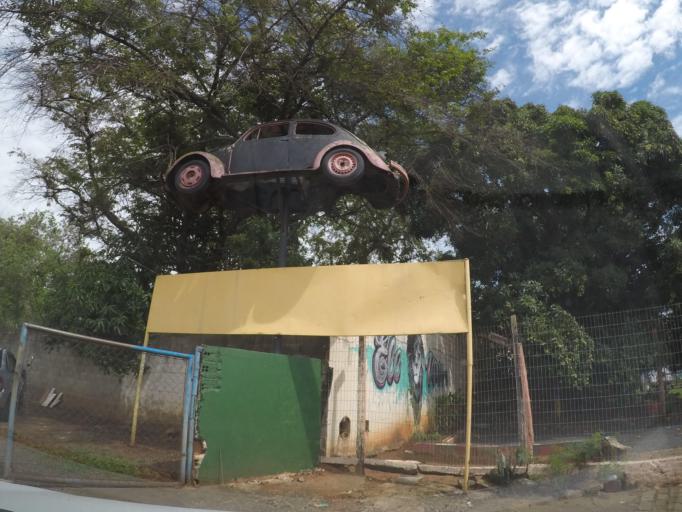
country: BR
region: Sao Paulo
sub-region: Hortolandia
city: Hortolandia
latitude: -22.8367
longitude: -47.1892
